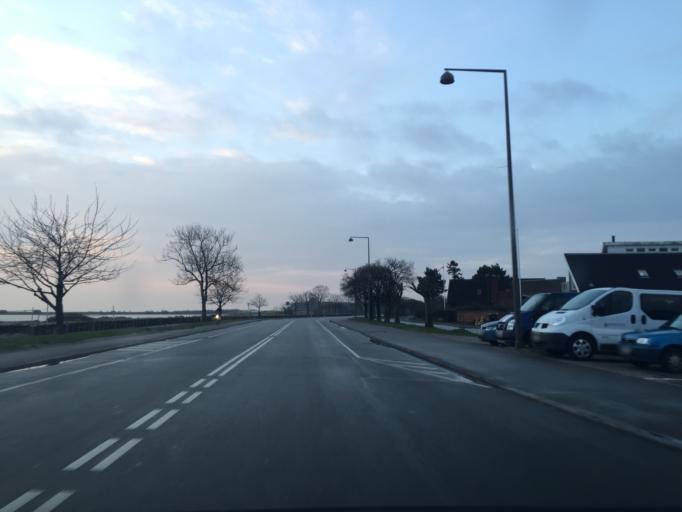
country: DK
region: Capital Region
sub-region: Kobenhavn
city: Christianshavn
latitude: 55.6567
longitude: 12.6369
